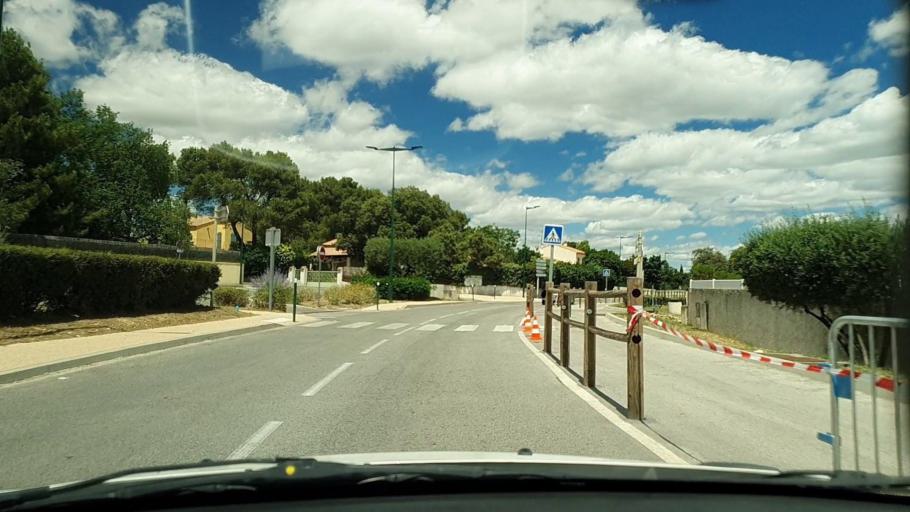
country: FR
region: Languedoc-Roussillon
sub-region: Departement du Gard
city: Poulx
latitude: 43.9008
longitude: 4.4209
